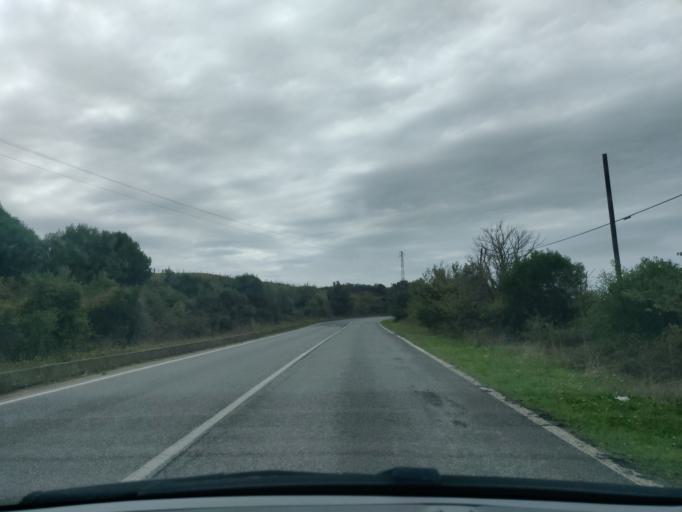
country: IT
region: Latium
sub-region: Citta metropolitana di Roma Capitale
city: Allumiere
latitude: 42.1163
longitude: 11.8612
